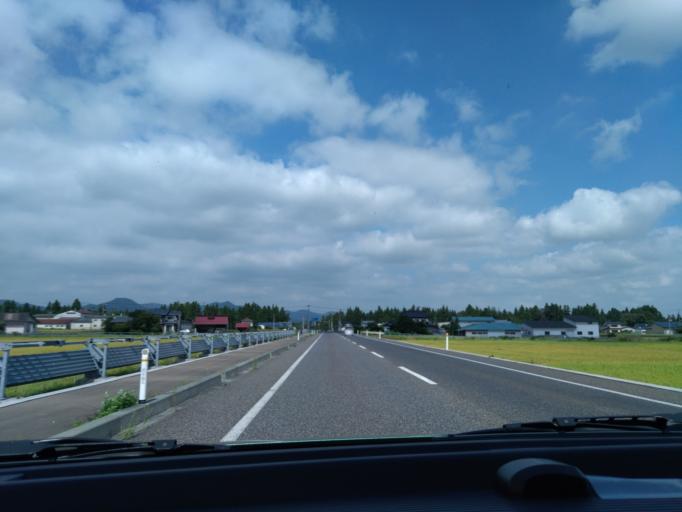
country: JP
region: Iwate
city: Hanamaki
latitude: 39.3705
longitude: 141.0569
